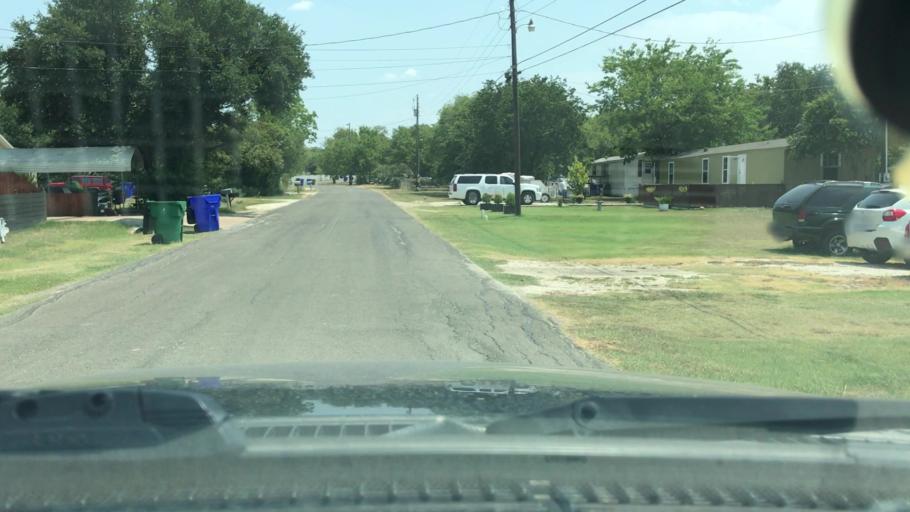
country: US
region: Texas
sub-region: Williamson County
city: Cedar Park
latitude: 30.5342
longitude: -97.8402
